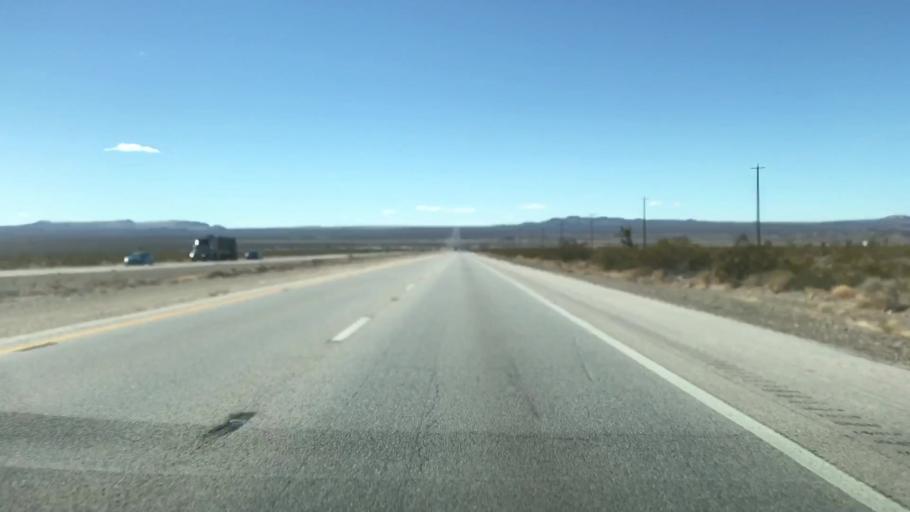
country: US
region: Nevada
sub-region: Clark County
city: Sandy Valley
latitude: 35.4549
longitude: -115.6441
